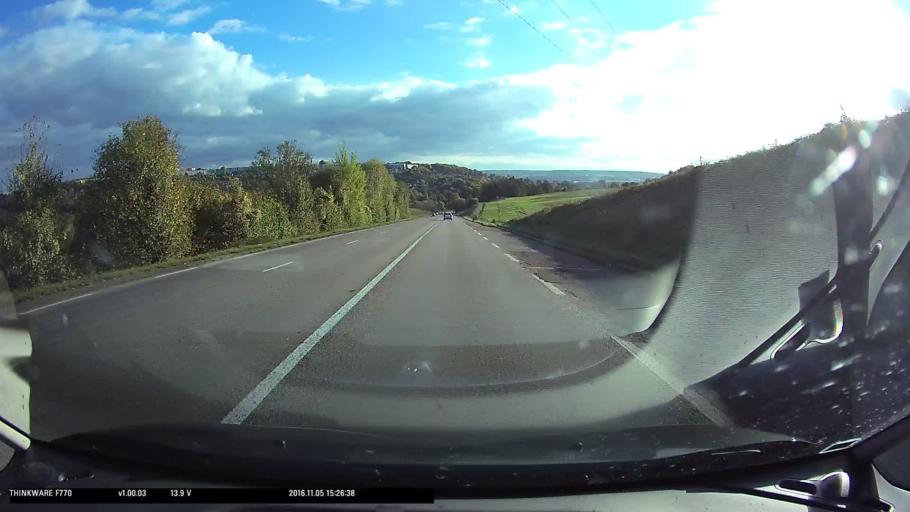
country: FR
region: Ile-de-France
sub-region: Departement des Yvelines
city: Meulan-en-Yvelines
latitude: 49.0214
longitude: 1.9098
